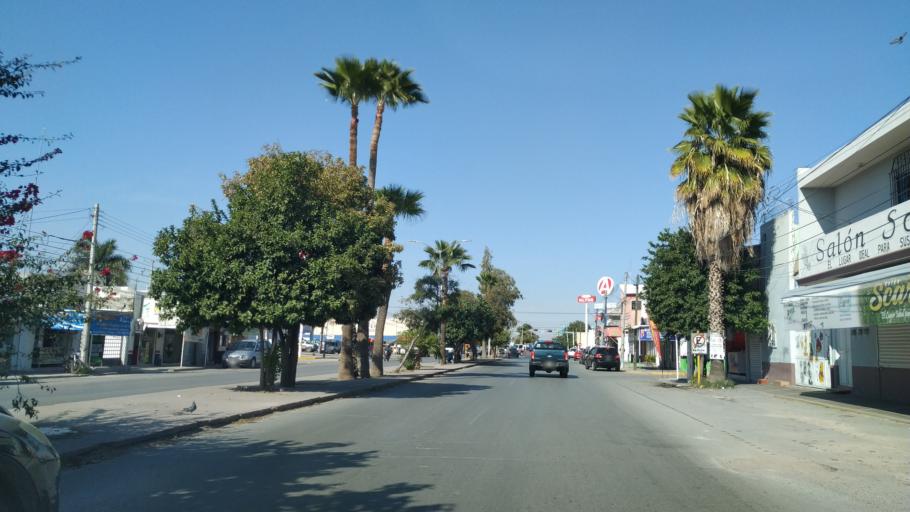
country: MX
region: Coahuila
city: Torreon
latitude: 25.5366
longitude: -103.3959
